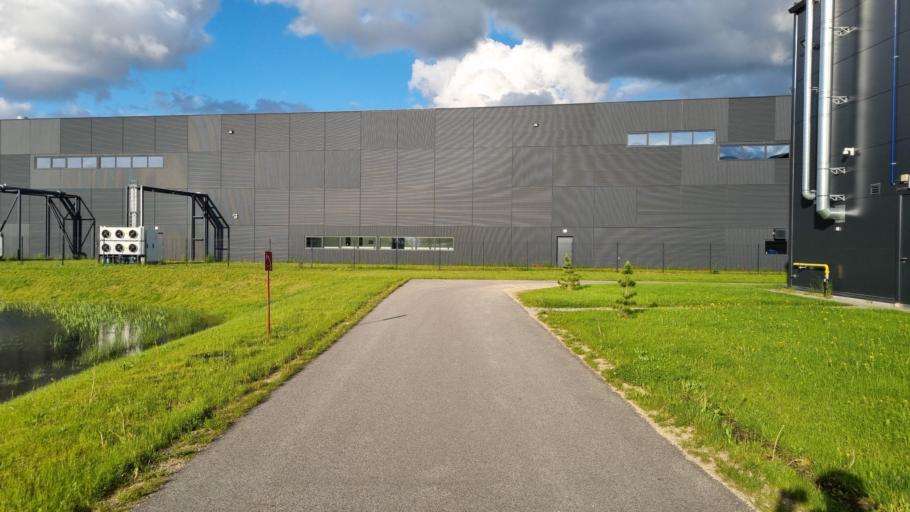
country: LV
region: Marupe
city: Marupe
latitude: 56.9215
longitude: 24.0013
